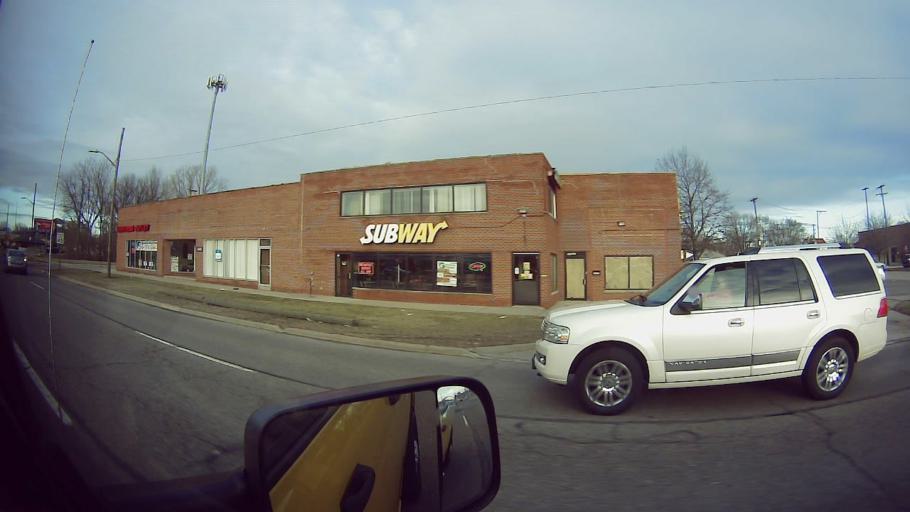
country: US
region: Michigan
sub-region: Wayne County
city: Taylor
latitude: 42.2705
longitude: -83.2702
